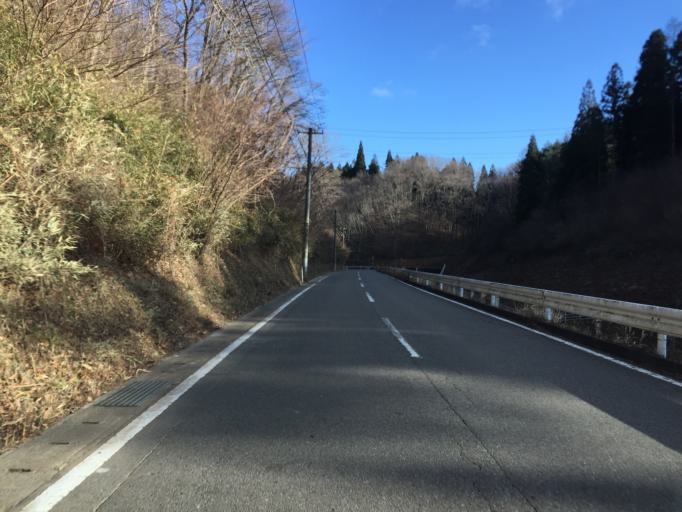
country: JP
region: Fukushima
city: Funehikimachi-funehiki
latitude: 37.2448
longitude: 140.6771
